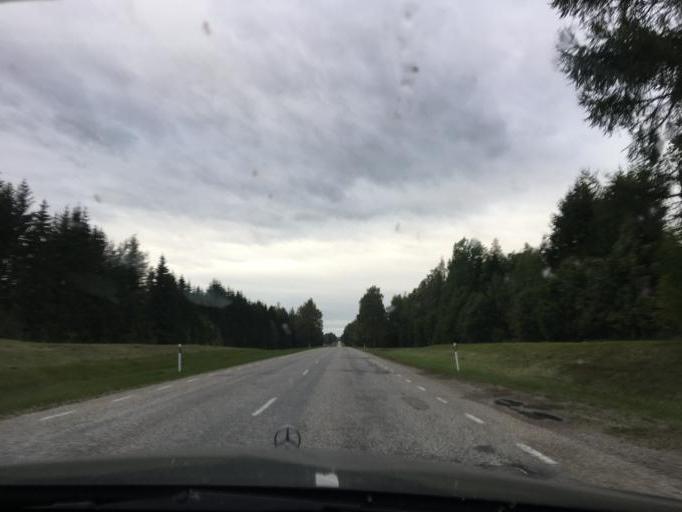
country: LV
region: Aluksnes Rajons
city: Aluksne
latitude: 57.5974
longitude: 27.2057
